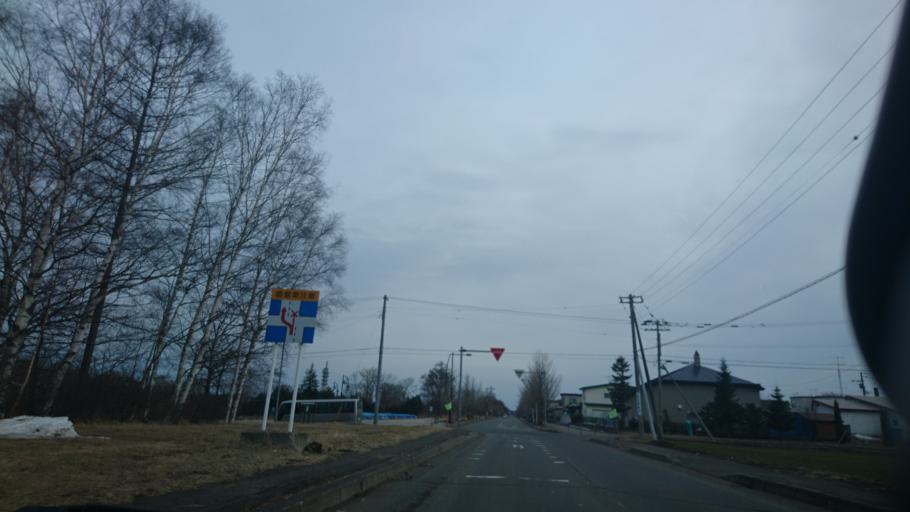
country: JP
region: Hokkaido
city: Otofuke
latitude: 42.9723
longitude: 143.1987
